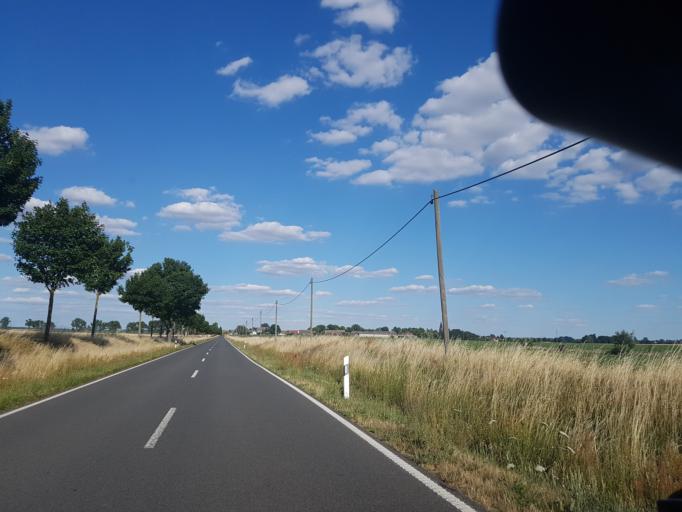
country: DE
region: Brandenburg
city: Juterbog
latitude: 51.9300
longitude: 13.1263
